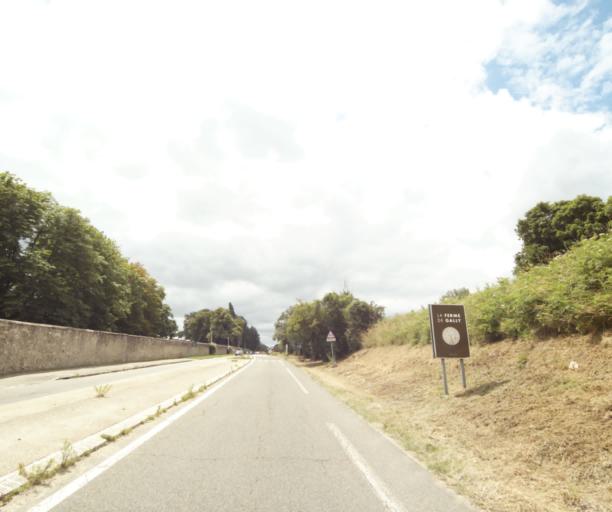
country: FR
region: Ile-de-France
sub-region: Departement des Yvelines
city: Saint-Cyr-l'Ecole
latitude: 48.8182
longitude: 2.0803
